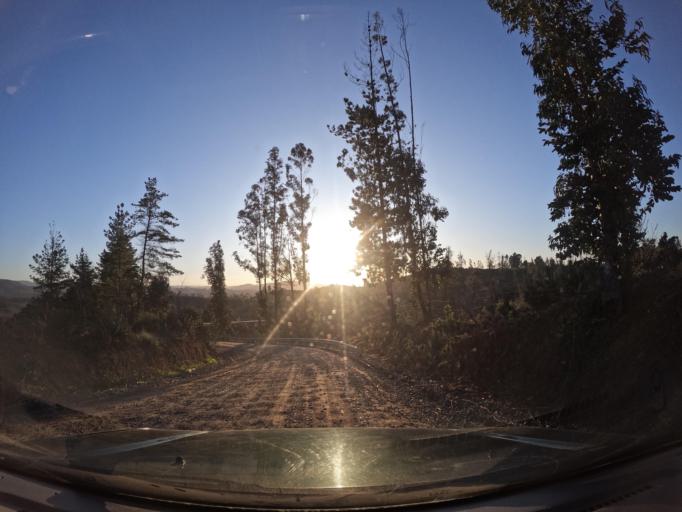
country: CL
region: Biobio
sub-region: Provincia de Concepcion
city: Chiguayante
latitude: -37.0097
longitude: -72.8903
